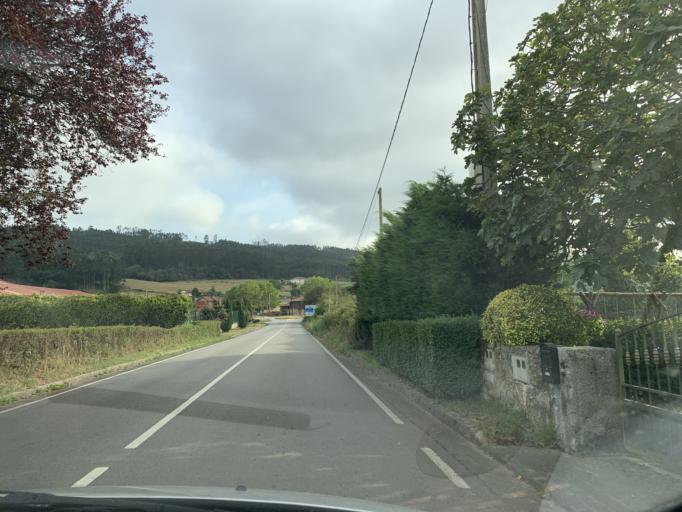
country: ES
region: Asturias
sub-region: Province of Asturias
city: Villaviciosa
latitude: 43.5219
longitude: -5.4387
